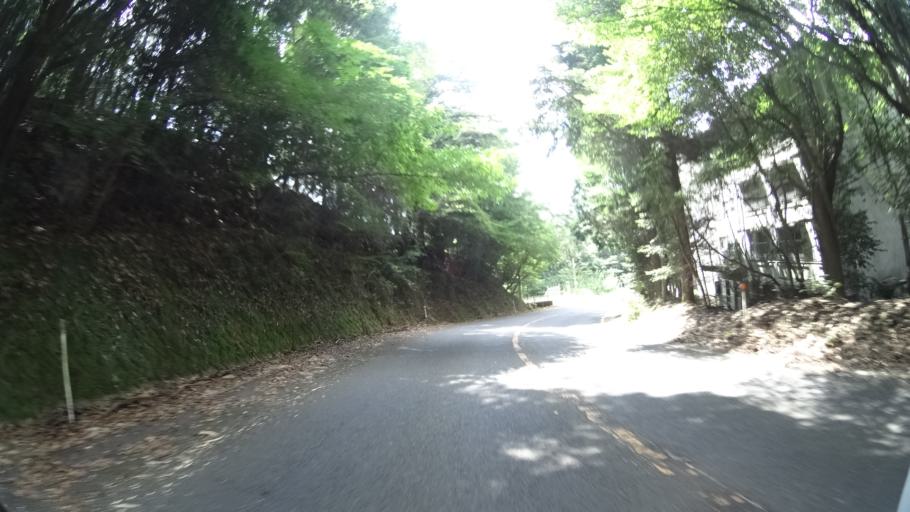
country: JP
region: Miyazaki
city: Kobayashi
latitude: 31.9029
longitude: 130.8367
